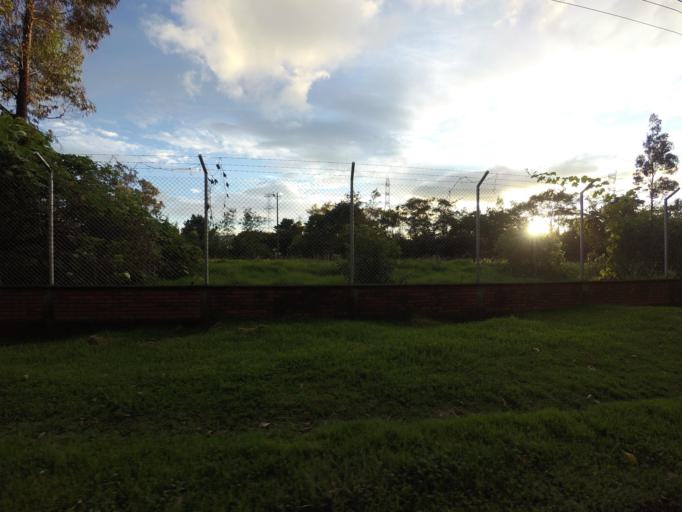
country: CO
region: Cundinamarca
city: Cota
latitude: 4.7787
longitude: -74.0265
